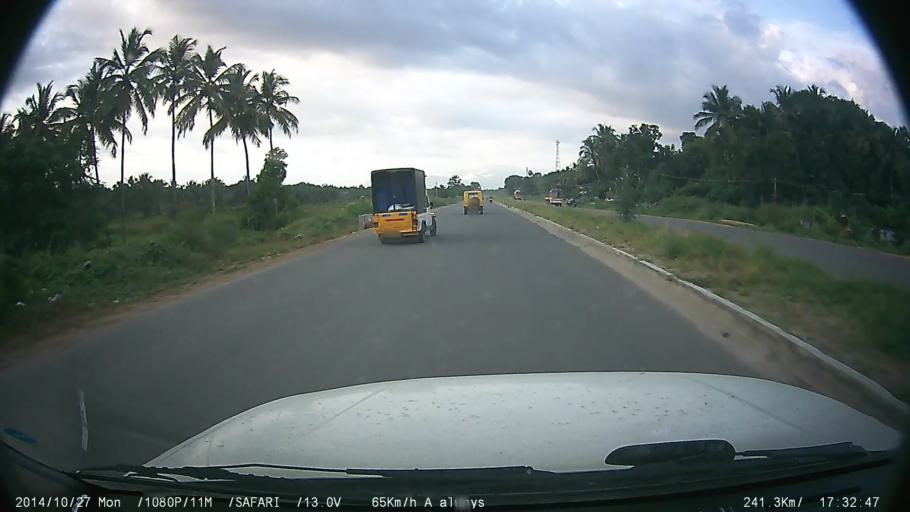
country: IN
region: Kerala
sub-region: Palakkad district
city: Palakkad
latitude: 10.6757
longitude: 76.5775
